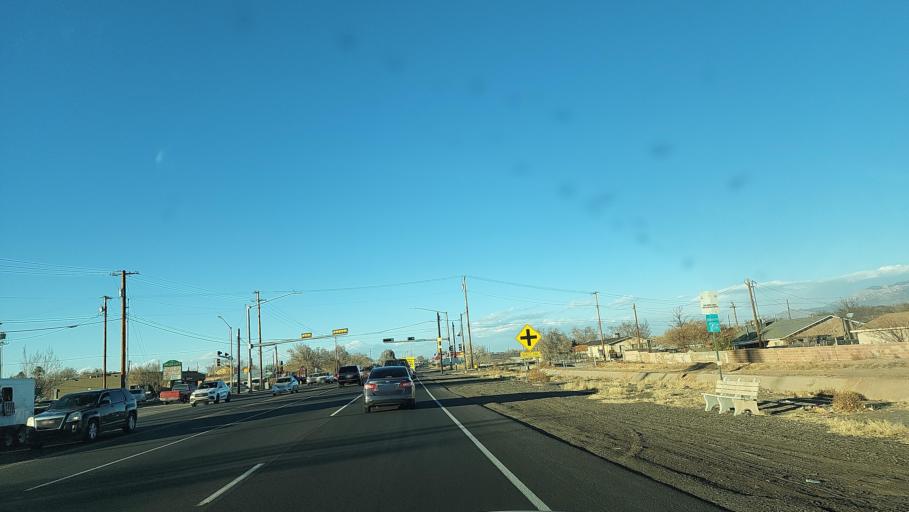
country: US
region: New Mexico
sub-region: Bernalillo County
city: South Valley
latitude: 35.0296
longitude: -106.7135
